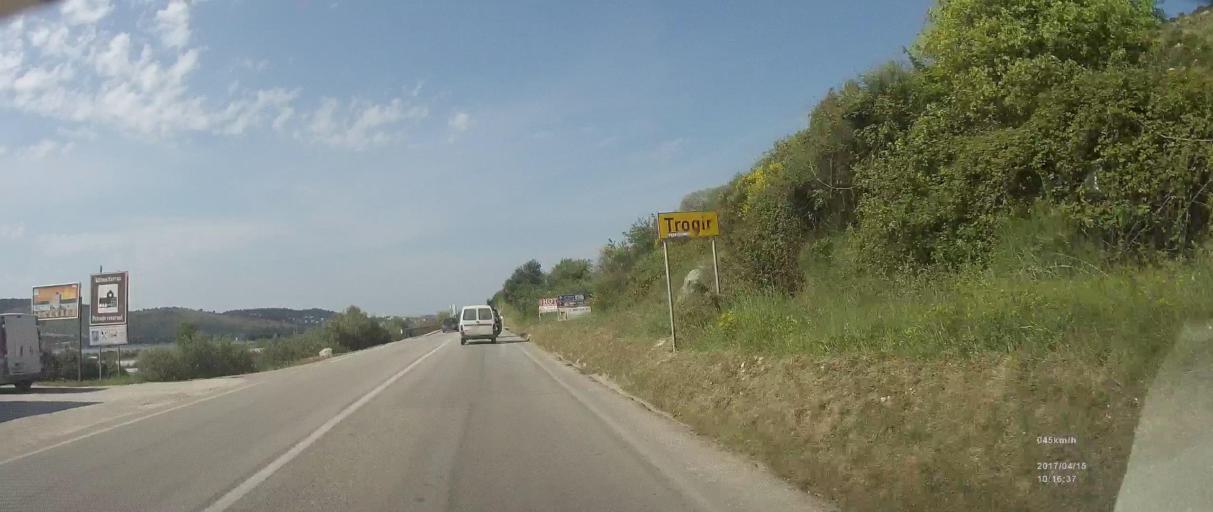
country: HR
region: Splitsko-Dalmatinska
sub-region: Grad Trogir
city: Trogir
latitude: 43.5303
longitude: 16.2769
